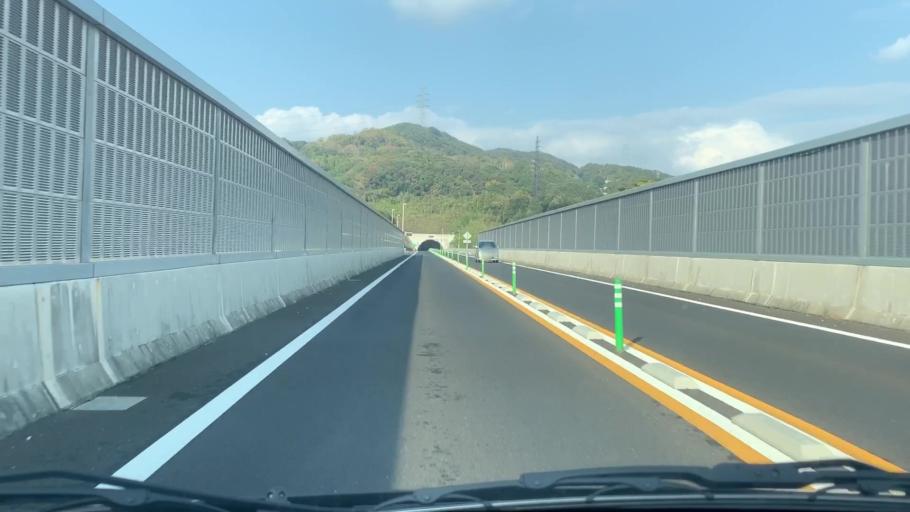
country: JP
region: Nagasaki
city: Sasebo
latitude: 33.0841
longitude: 129.7769
